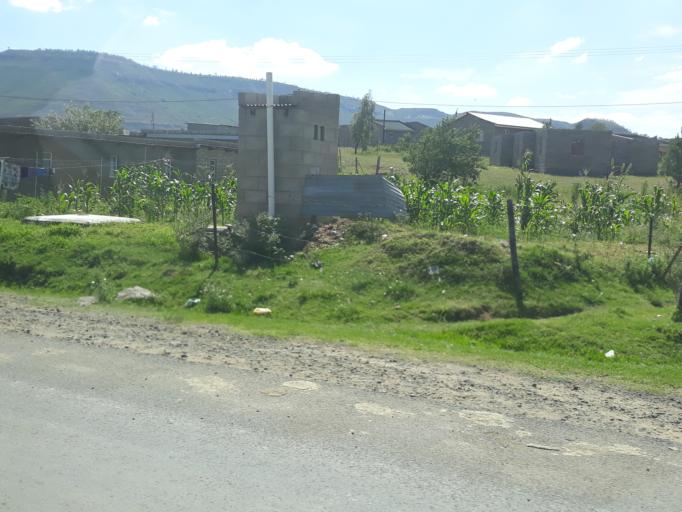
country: LS
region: Mohale's Hoek District
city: Mohale's Hoek
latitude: -30.1095
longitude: 27.4690
